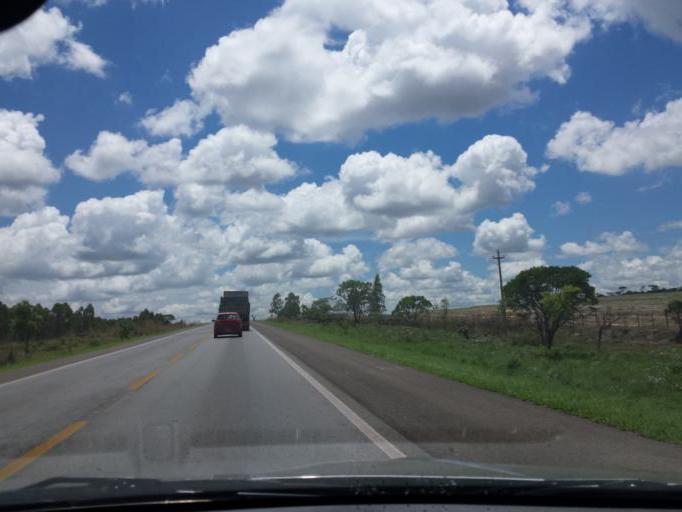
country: BR
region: Goias
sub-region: Cristalina
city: Cristalina
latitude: -16.7285
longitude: -47.6320
